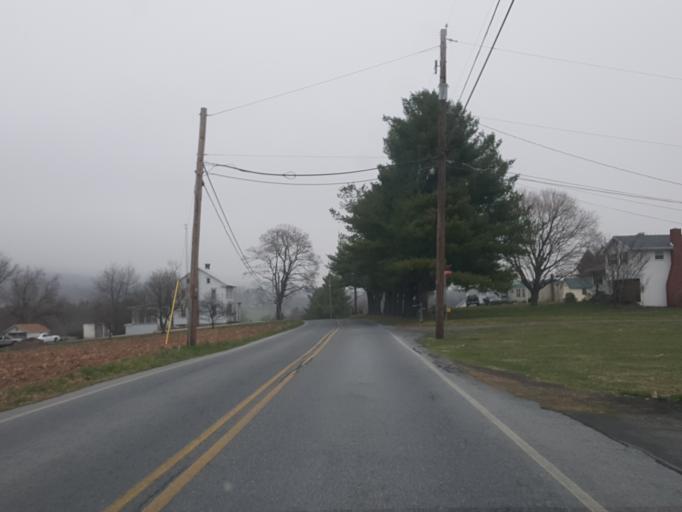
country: US
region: Pennsylvania
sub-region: Schuylkill County
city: Tower City
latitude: 40.5344
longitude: -76.4822
